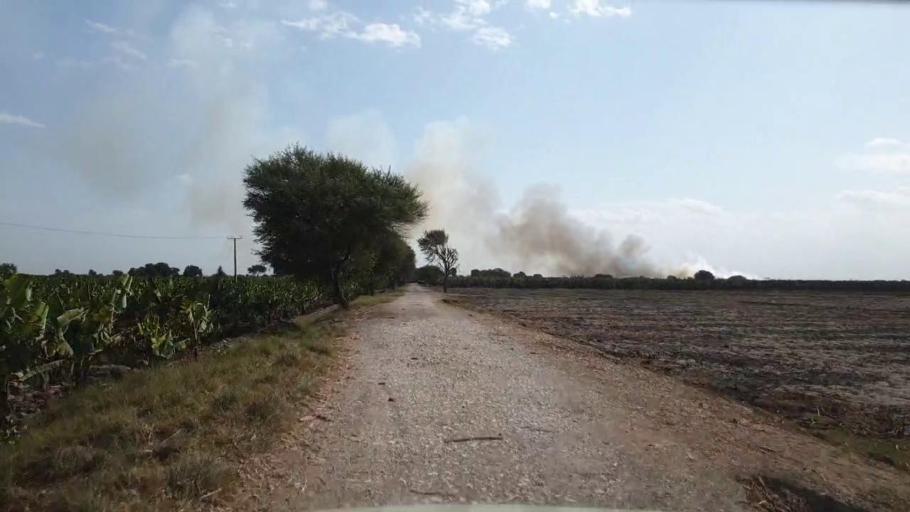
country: PK
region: Sindh
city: Matiari
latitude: 25.5554
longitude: 68.5577
